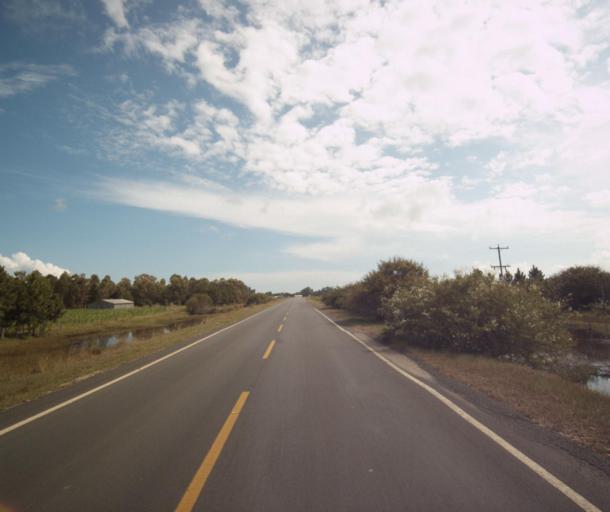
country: BR
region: Rio Grande do Sul
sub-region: Sao Lourenco Do Sul
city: Sao Lourenco do Sul
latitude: -31.6052
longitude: -51.3852
